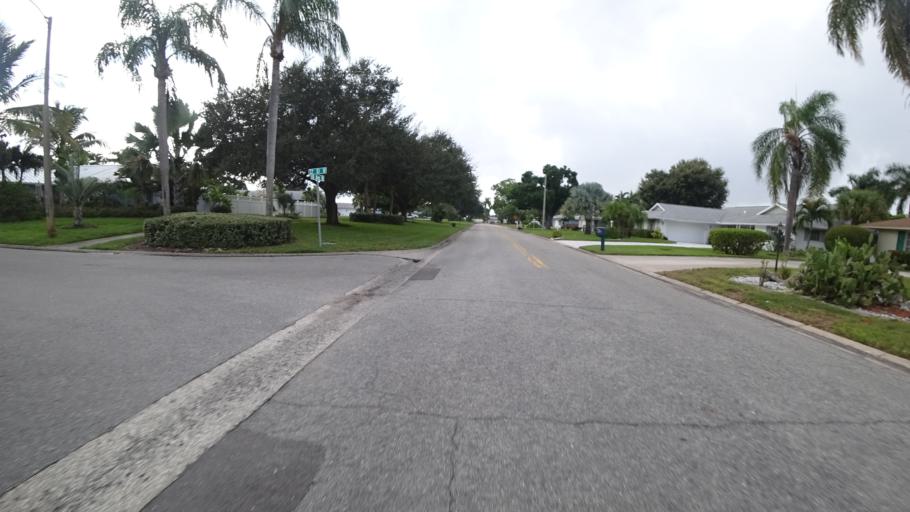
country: US
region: Florida
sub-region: Manatee County
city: West Bradenton
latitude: 27.4836
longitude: -82.6334
